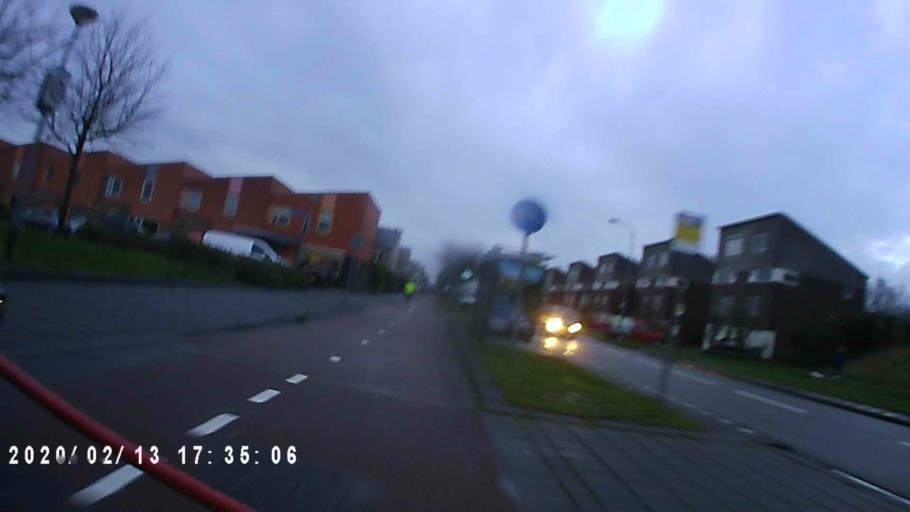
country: NL
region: Groningen
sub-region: Gemeente Groningen
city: Groningen
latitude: 53.2235
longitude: 6.5135
